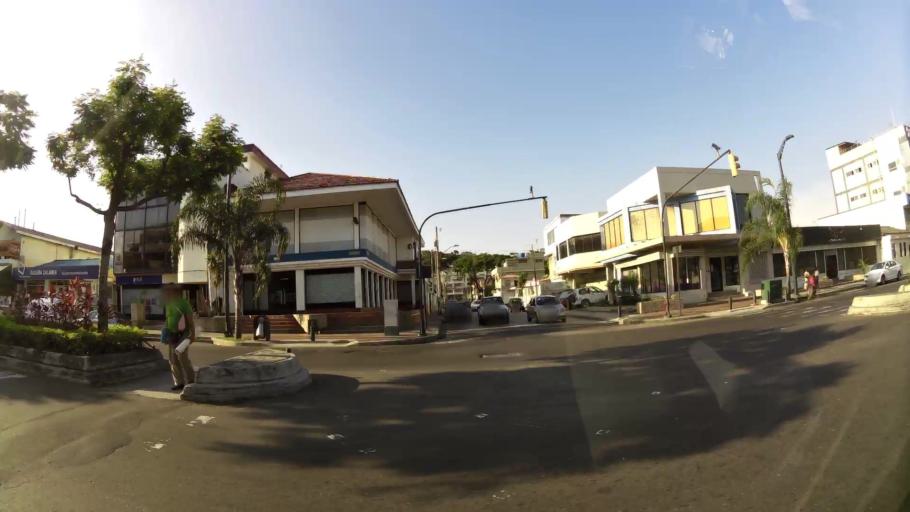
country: EC
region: Guayas
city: Guayaquil
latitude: -2.1617
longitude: -79.9156
